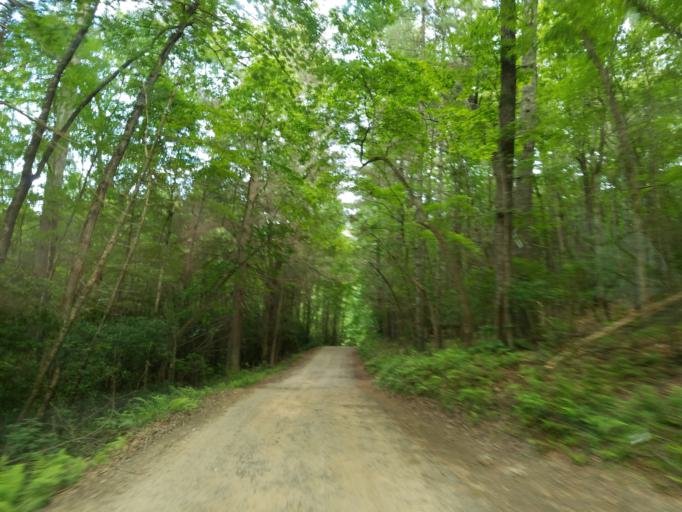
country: US
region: Georgia
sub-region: Fannin County
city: Blue Ridge
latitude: 34.7638
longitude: -84.1686
